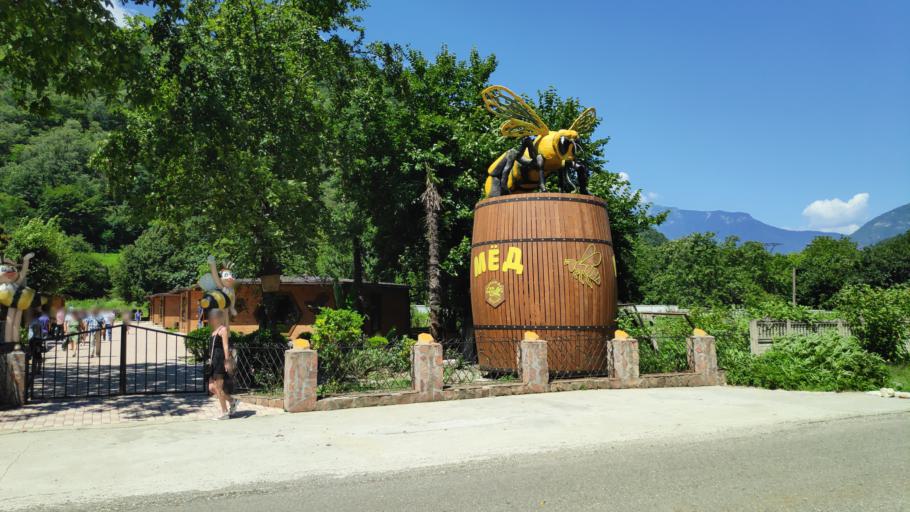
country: GE
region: Abkhazia
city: Gagra
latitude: 43.2831
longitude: 40.3987
